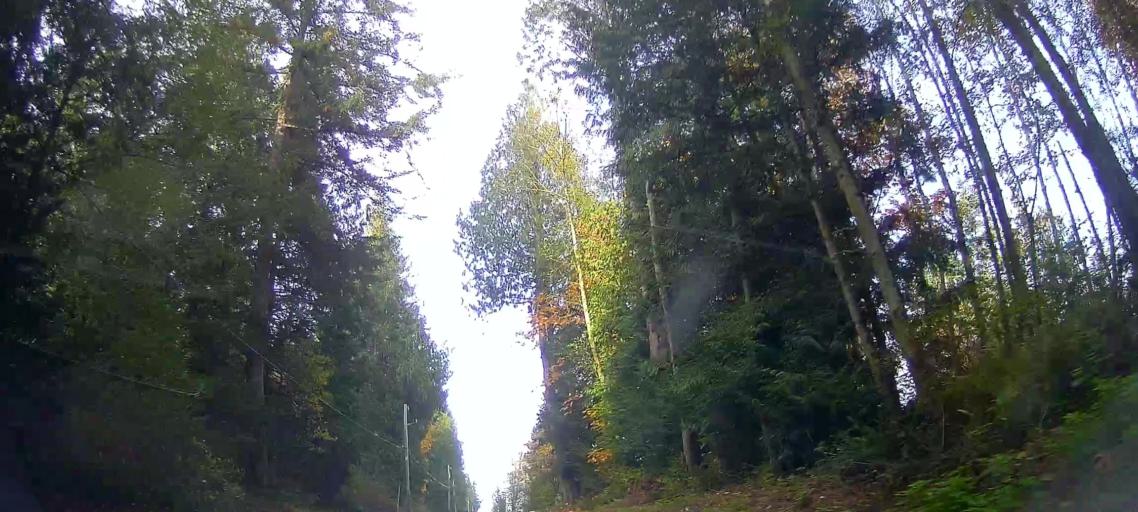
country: US
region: Washington
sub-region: Snohomish County
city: Stanwood
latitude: 48.2635
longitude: -122.3414
